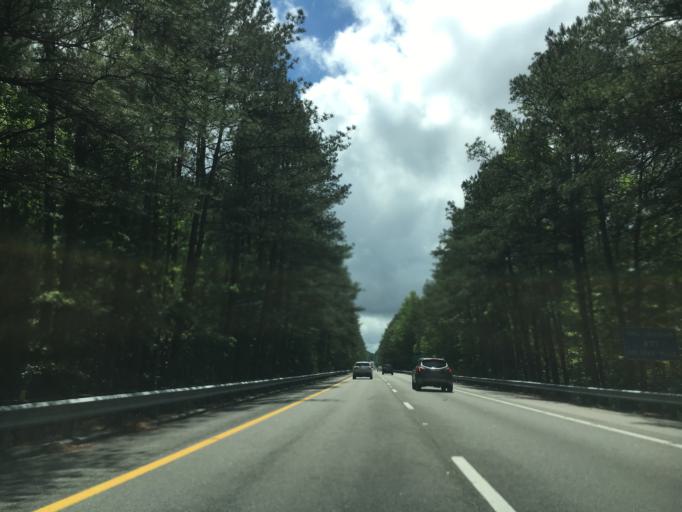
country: US
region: Virginia
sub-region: Brunswick County
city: Lawrenceville
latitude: 36.8158
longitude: -77.9705
